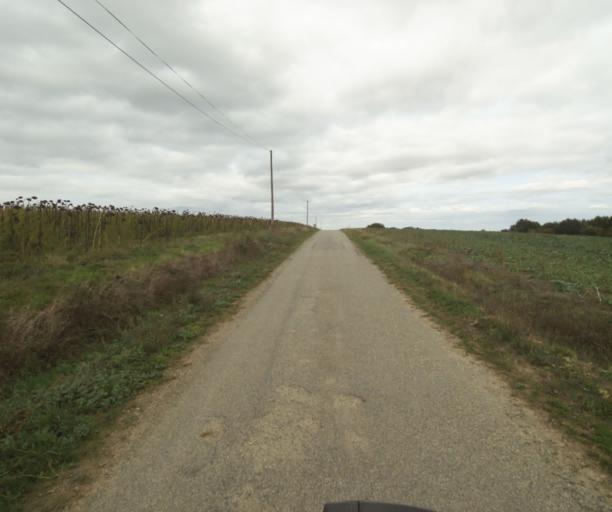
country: FR
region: Midi-Pyrenees
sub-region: Departement du Tarn-et-Garonne
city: Beaumont-de-Lomagne
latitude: 43.8444
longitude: 1.0968
